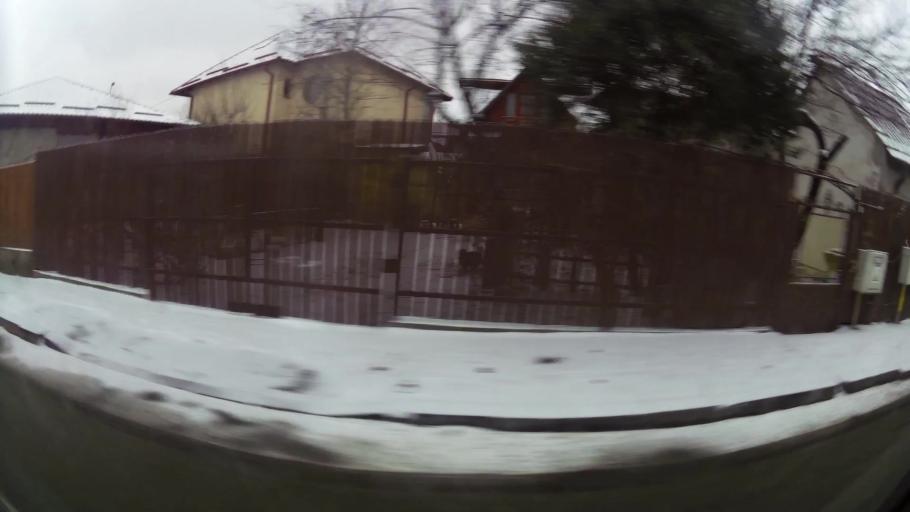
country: RO
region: Prahova
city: Ploiesti
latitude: 44.9363
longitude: 26.0436
